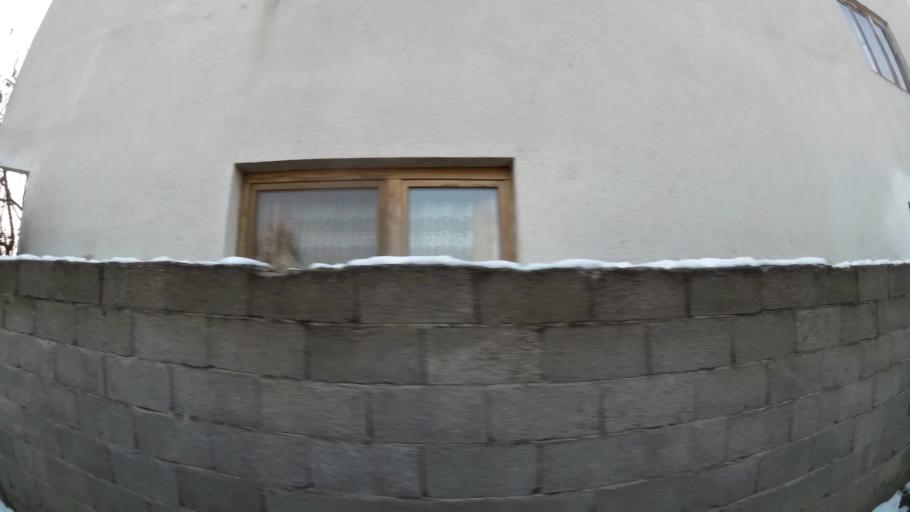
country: MK
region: Aracinovo
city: Arachinovo
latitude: 42.0124
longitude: 21.5288
